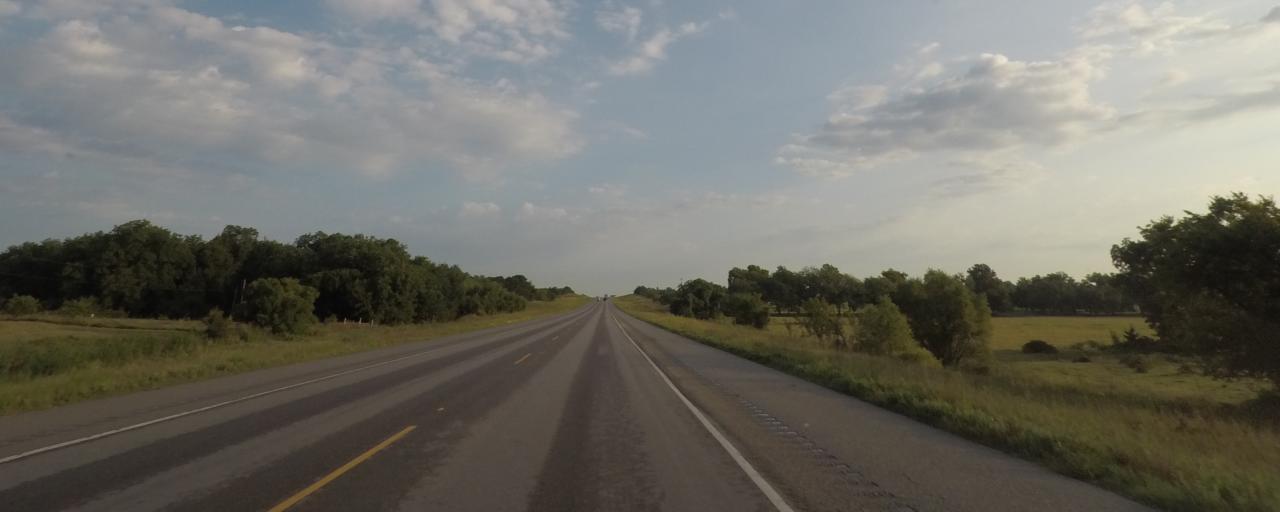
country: US
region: Oklahoma
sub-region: Stephens County
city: Meridian
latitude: 34.4421
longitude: -97.9741
